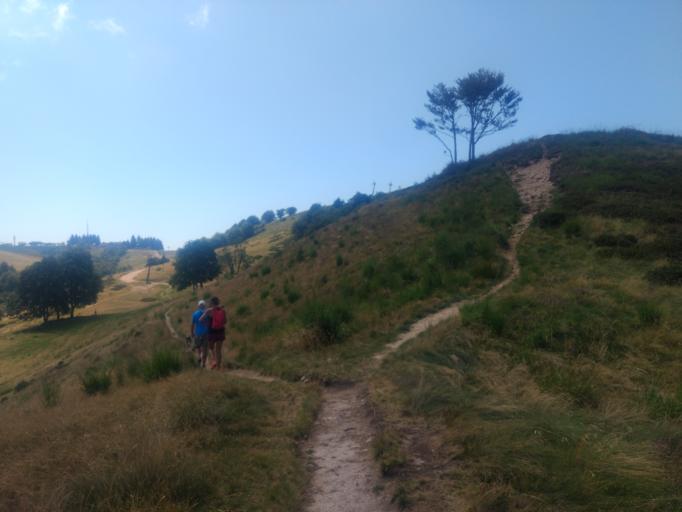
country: IT
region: Piedmont
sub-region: Provincia Verbano-Cusio-Ossola
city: Gabbio-Cereda-Ramate
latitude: 45.8879
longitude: 8.4480
